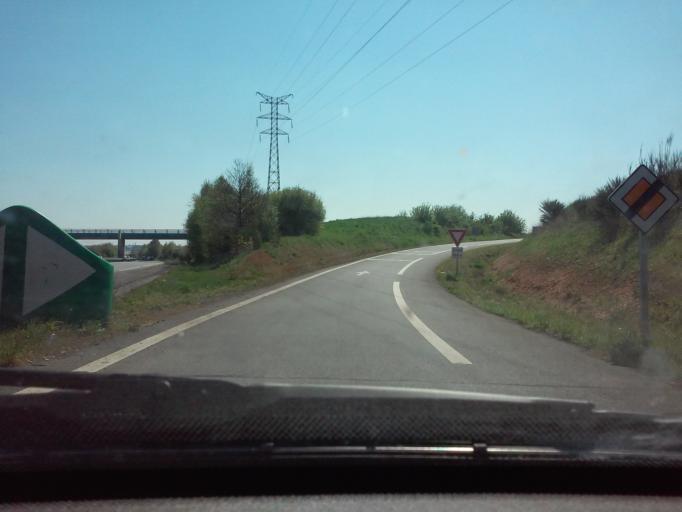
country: FR
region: Brittany
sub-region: Departement d'Ille-et-Vilaine
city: La Chapelle-des-Fougeretz
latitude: 48.1761
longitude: -1.7179
